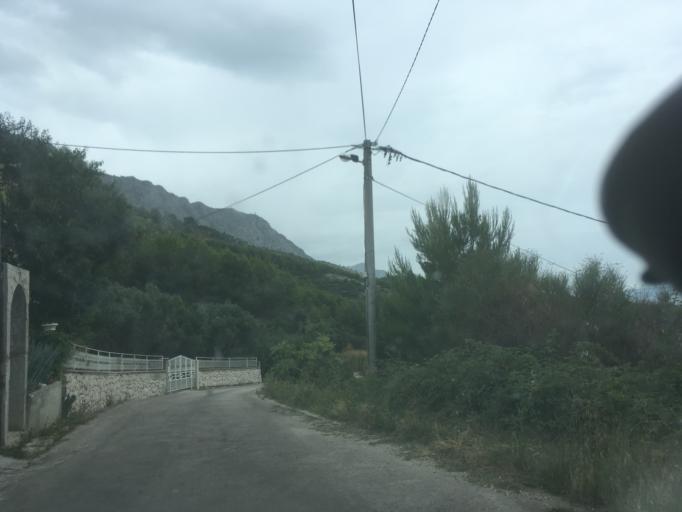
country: HR
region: Splitsko-Dalmatinska
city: Jesenice
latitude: 43.4584
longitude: 16.6180
